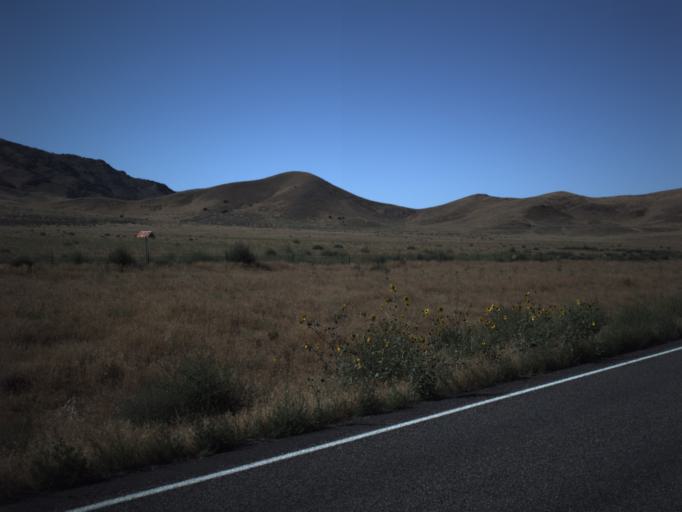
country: US
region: Utah
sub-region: Millard County
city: Delta
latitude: 39.6616
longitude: -112.2793
